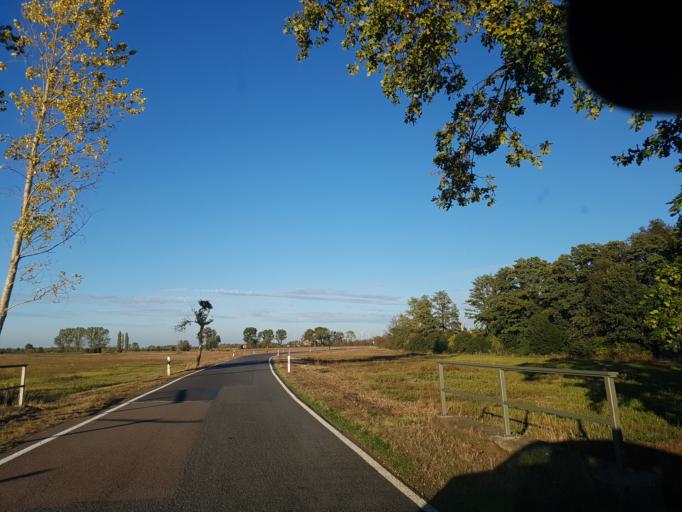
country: DE
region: Brandenburg
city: Muhlberg
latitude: 51.4971
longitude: 13.2681
